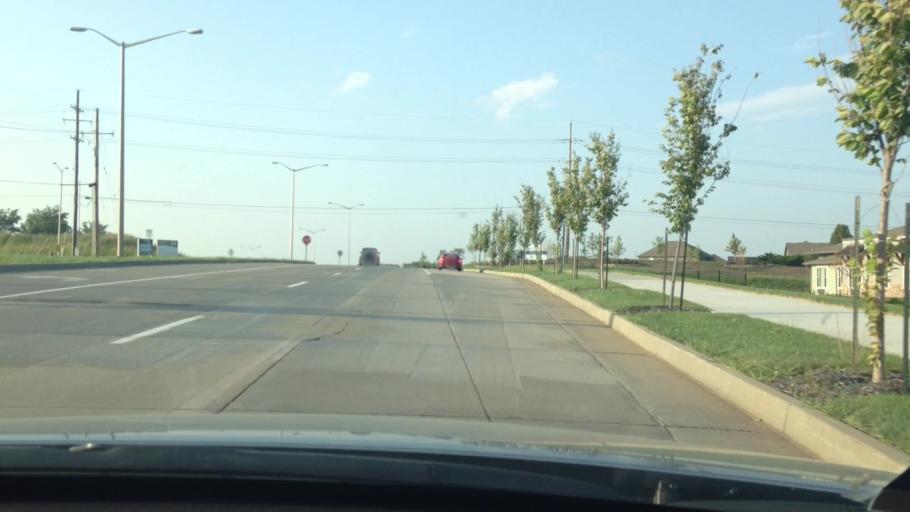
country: US
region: Missouri
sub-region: Platte County
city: Weatherby Lake
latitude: 39.2601
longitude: -94.6493
